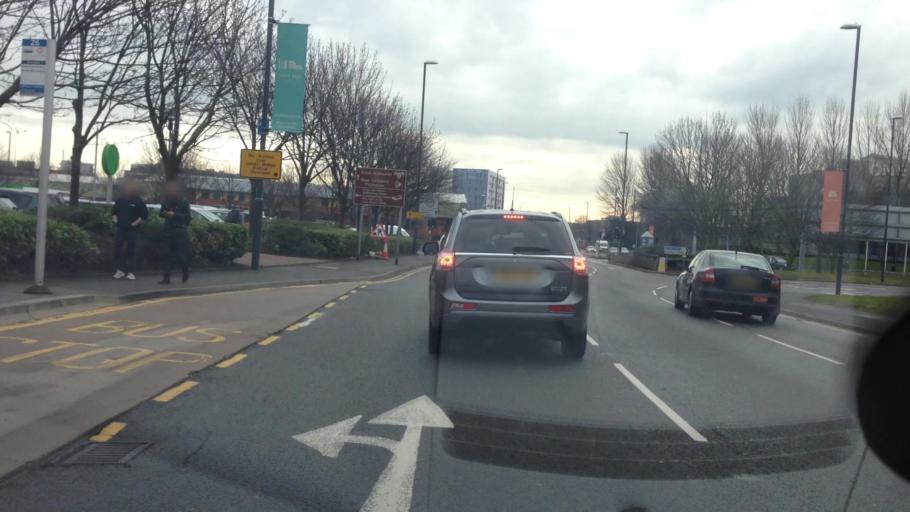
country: GB
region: England
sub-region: City and Borough of Leeds
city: Leeds
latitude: 53.7915
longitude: -1.5454
